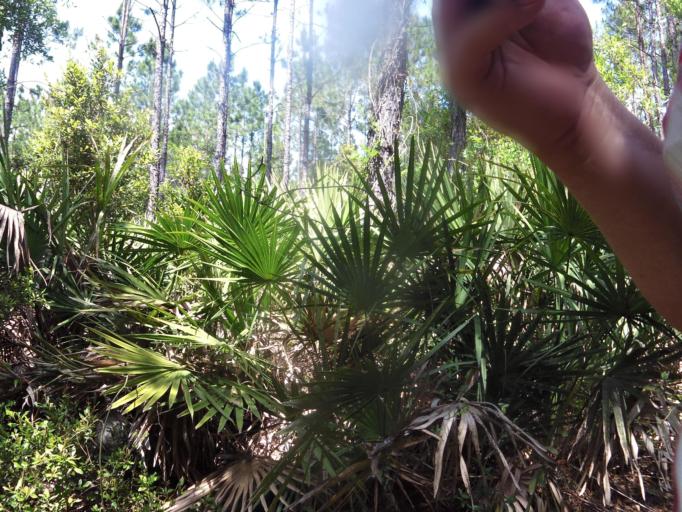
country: US
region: Florida
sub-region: Nassau County
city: Yulee
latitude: 30.4923
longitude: -81.4993
